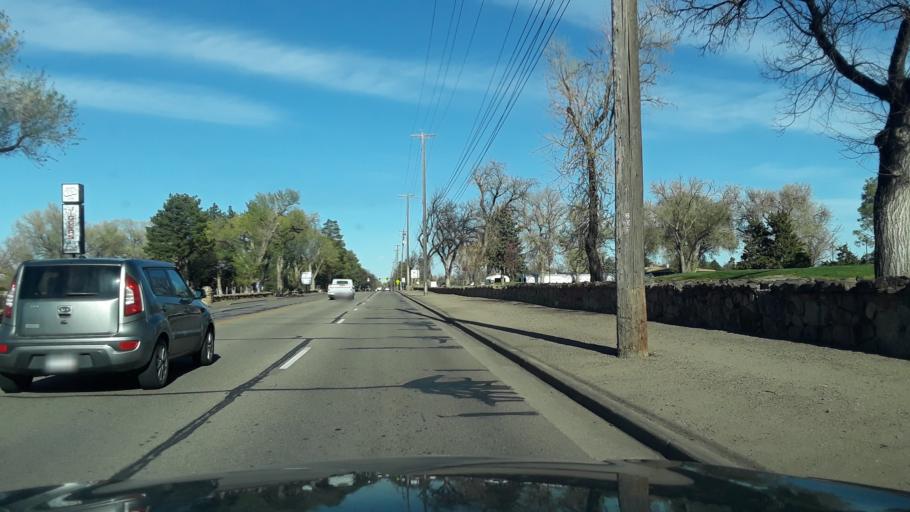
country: US
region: Colorado
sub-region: Pueblo County
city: Pueblo
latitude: 38.2584
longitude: -104.6580
